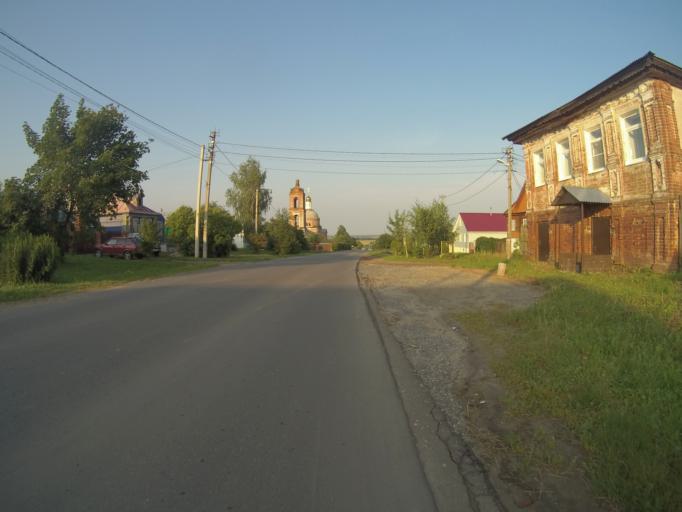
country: RU
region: Vladimir
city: Bogolyubovo
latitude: 56.2978
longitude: 40.5660
